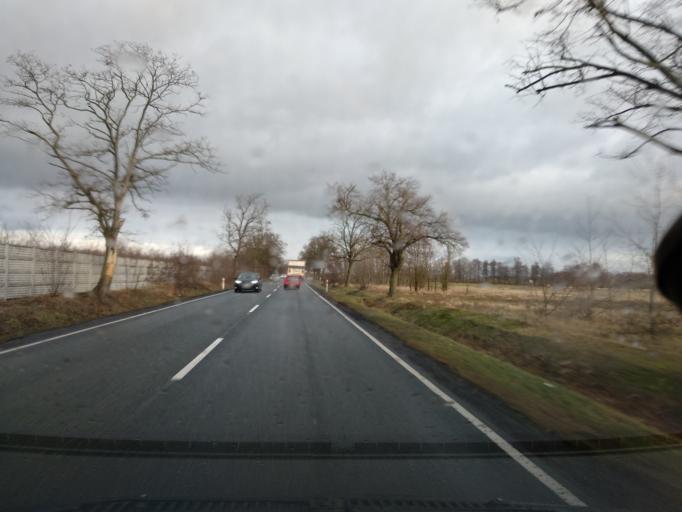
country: PL
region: Greater Poland Voivodeship
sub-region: Powiat koninski
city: Stare Miasto
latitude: 52.1321
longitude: 18.1824
